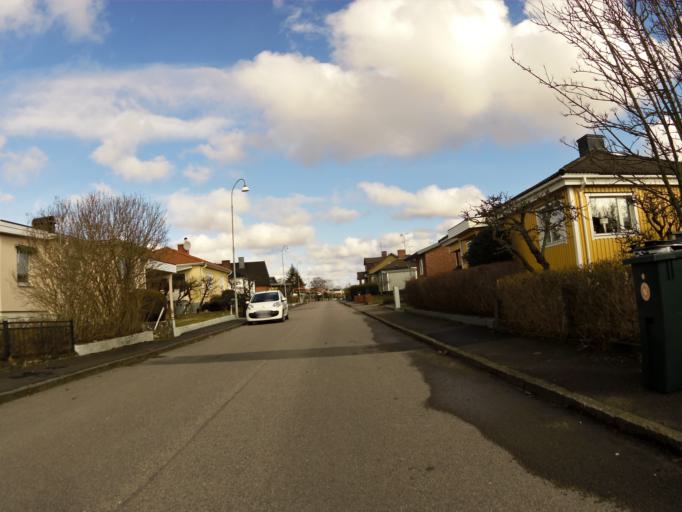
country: SE
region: Halland
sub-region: Halmstads Kommun
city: Halmstad
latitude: 56.6804
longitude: 12.8750
